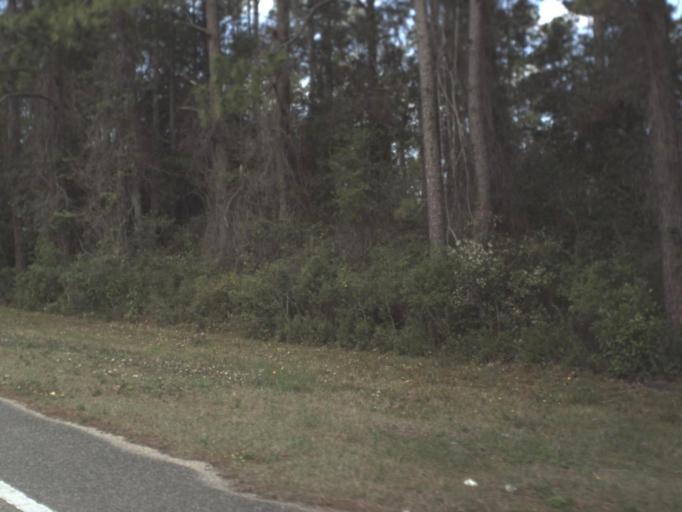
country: US
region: Florida
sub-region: Gulf County
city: Port Saint Joe
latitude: 29.7364
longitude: -85.1661
